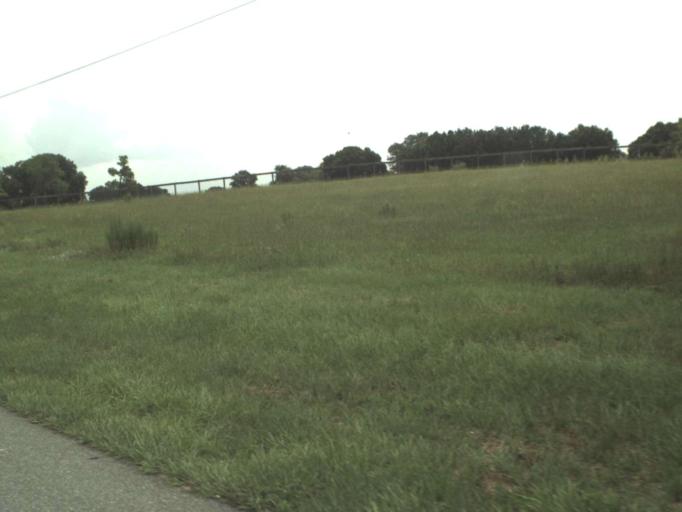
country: US
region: Florida
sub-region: Sumter County
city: Lake Panasoffkee
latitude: 28.7243
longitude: -82.0843
